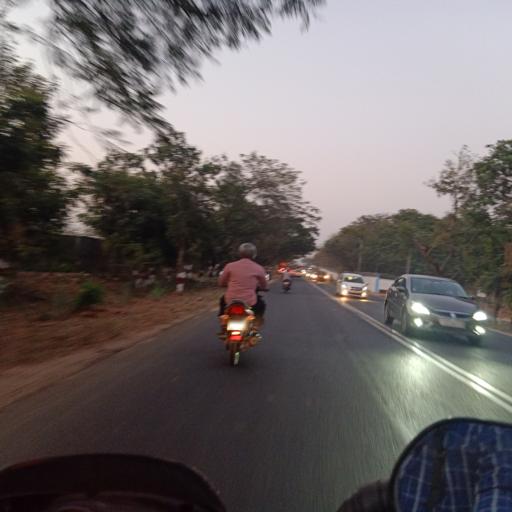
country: IN
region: Telangana
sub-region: Rangareddi
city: Secunderabad
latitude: 17.5508
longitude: 78.5359
